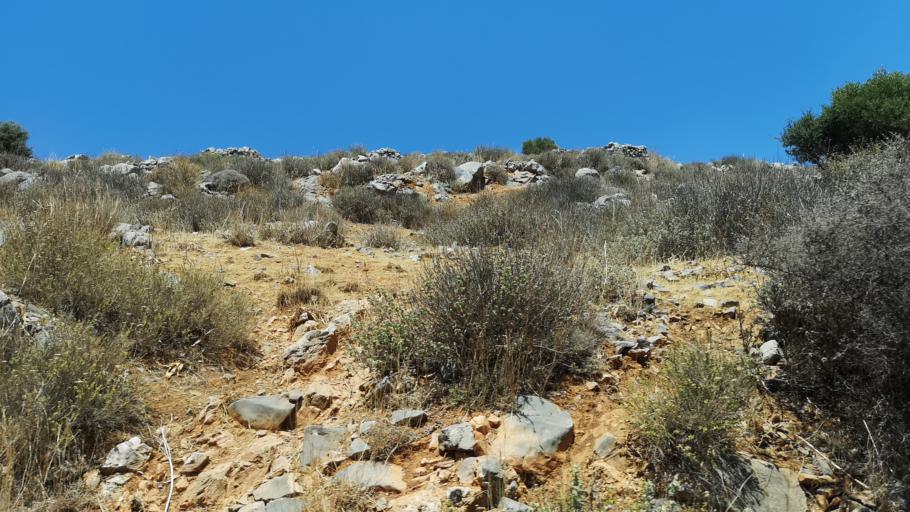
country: GR
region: Crete
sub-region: Nomos Lasithiou
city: Neapoli
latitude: 35.2521
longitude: 25.6325
